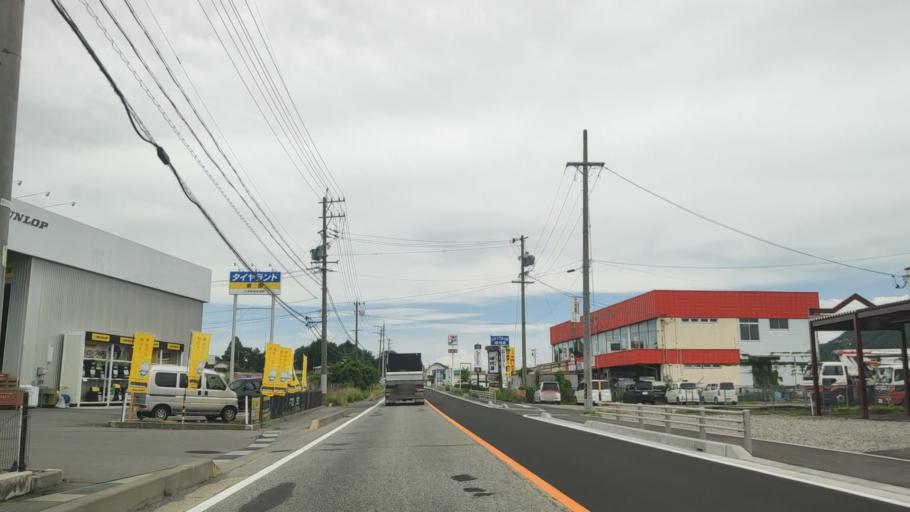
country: JP
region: Nagano
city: Komoro
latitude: 36.3473
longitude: 138.3692
